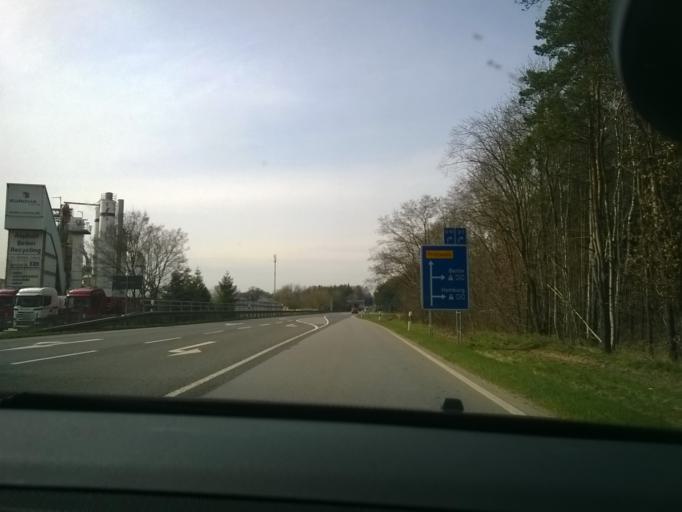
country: DE
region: Brandenburg
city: Heiligengrabe
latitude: 53.1492
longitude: 12.4125
